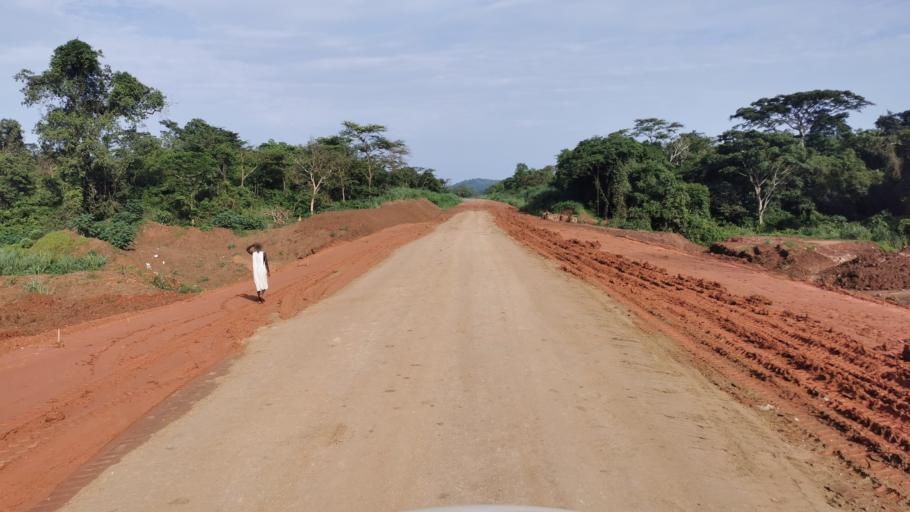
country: ET
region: Gambela
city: Gambela
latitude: 7.7742
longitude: 34.6460
